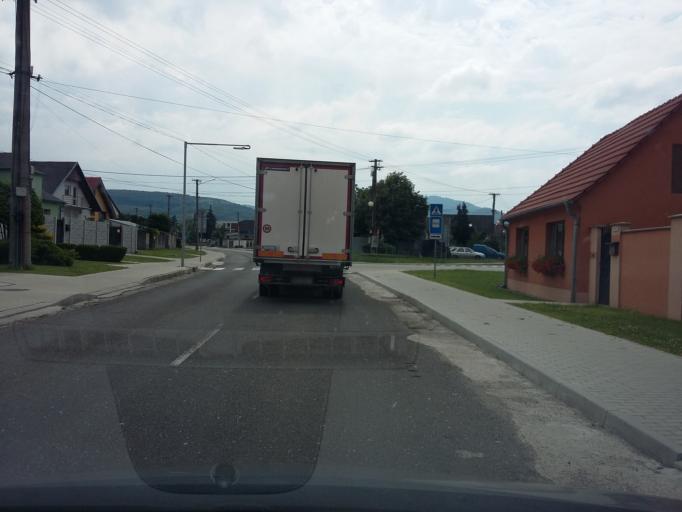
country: SK
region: Bratislavsky
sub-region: Okres Malacky
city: Malacky
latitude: 48.4581
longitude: 17.1678
